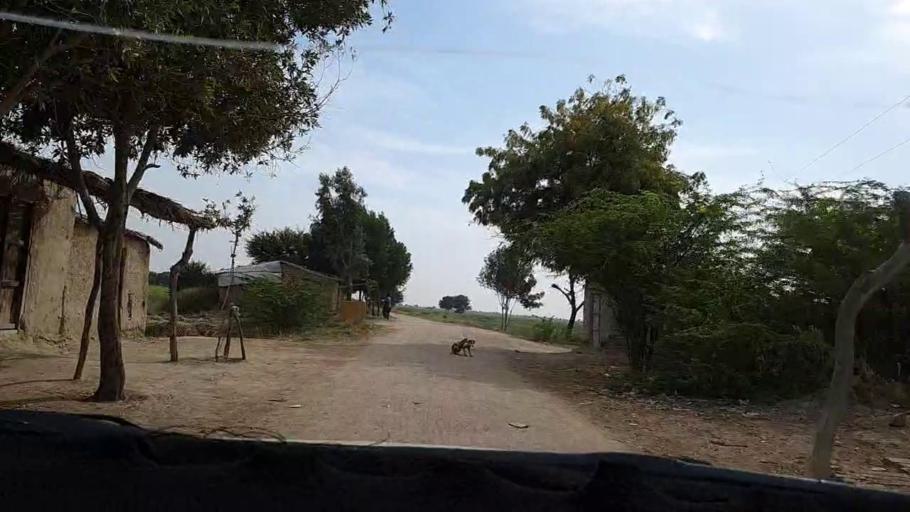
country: PK
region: Sindh
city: Pithoro
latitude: 25.5501
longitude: 69.3294
